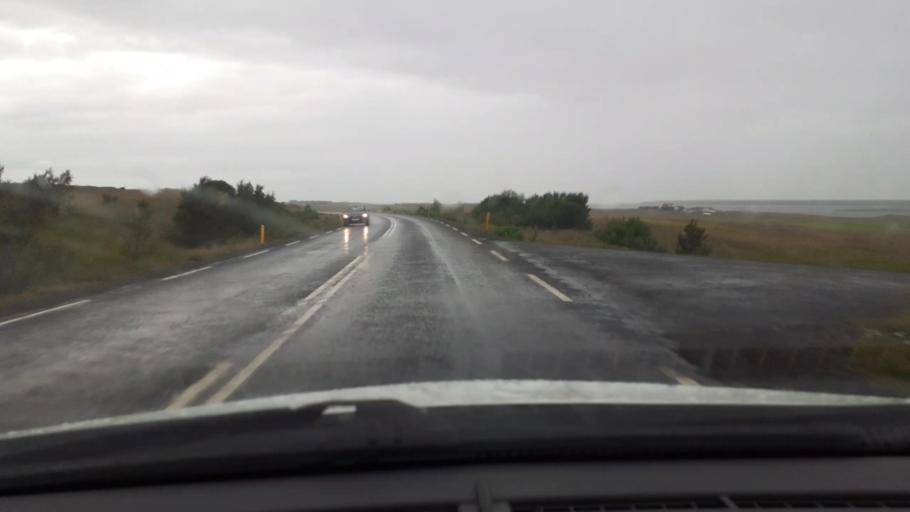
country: IS
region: West
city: Borgarnes
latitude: 64.3657
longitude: -21.9059
